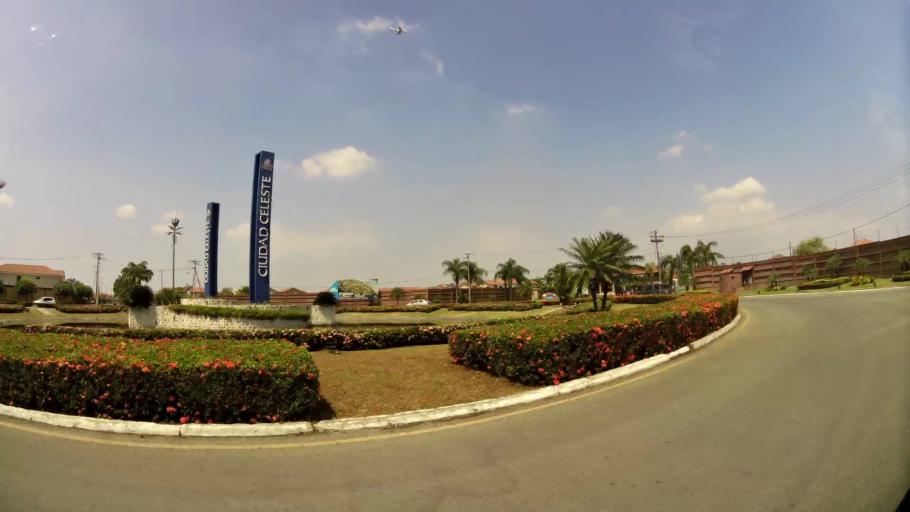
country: EC
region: Guayas
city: Eloy Alfaro
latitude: -2.0722
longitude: -79.8420
